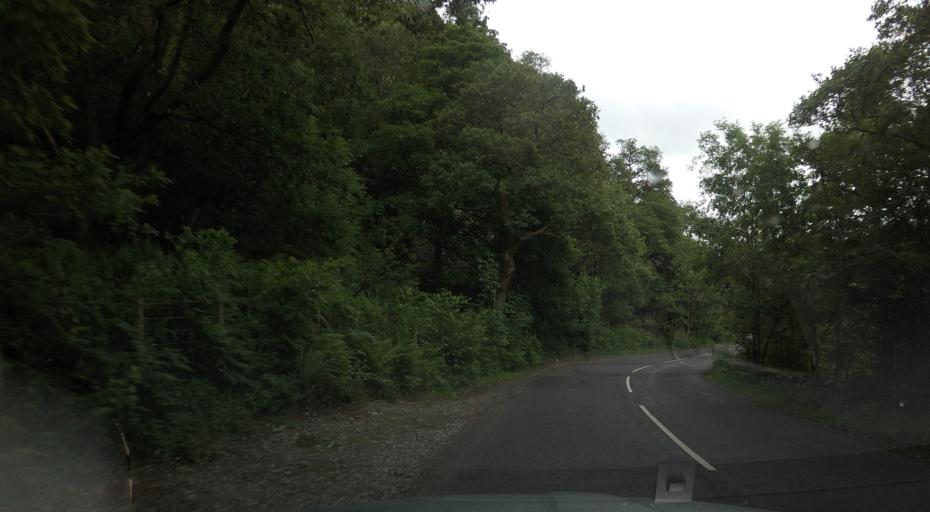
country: GB
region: England
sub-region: Cumbria
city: Keswick
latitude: 54.5362
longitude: -3.1539
